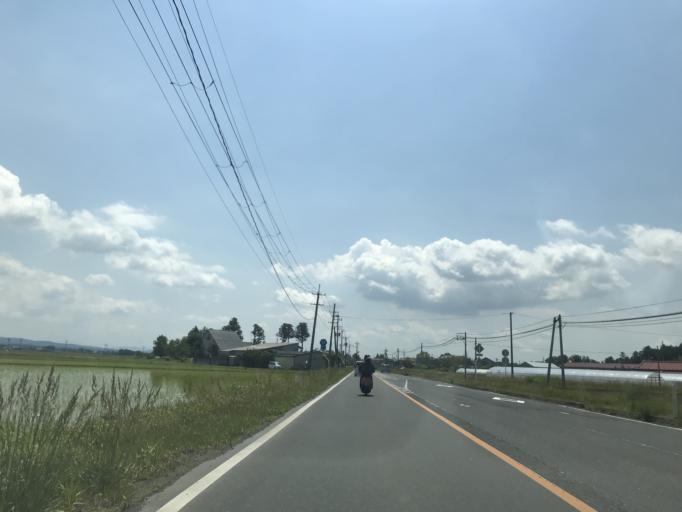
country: JP
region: Miyagi
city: Kogota
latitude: 38.5682
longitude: 141.0434
